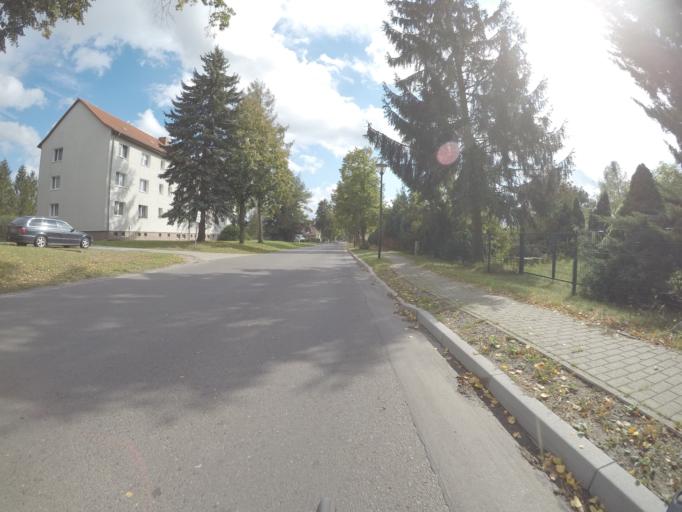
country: DE
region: Brandenburg
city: Werftpfuhl
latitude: 52.6029
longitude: 13.8098
